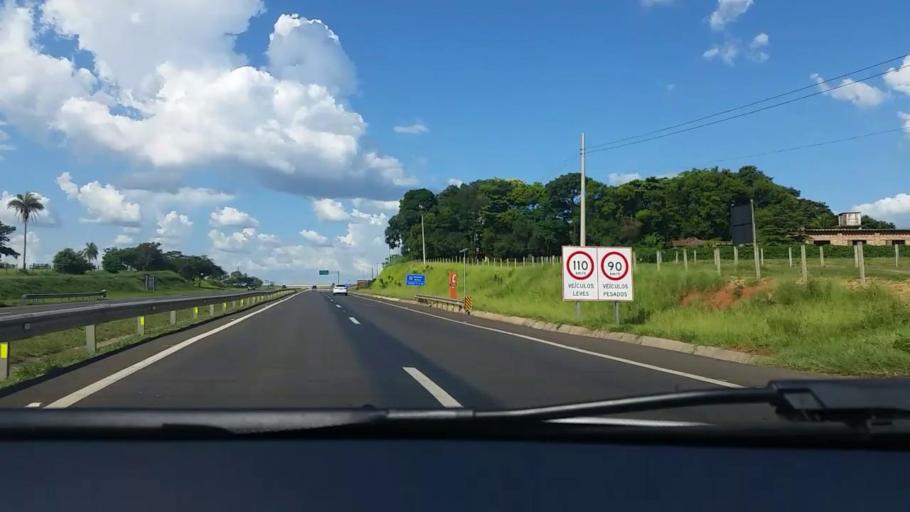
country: BR
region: Sao Paulo
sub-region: Bauru
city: Bauru
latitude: -22.3816
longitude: -49.0660
